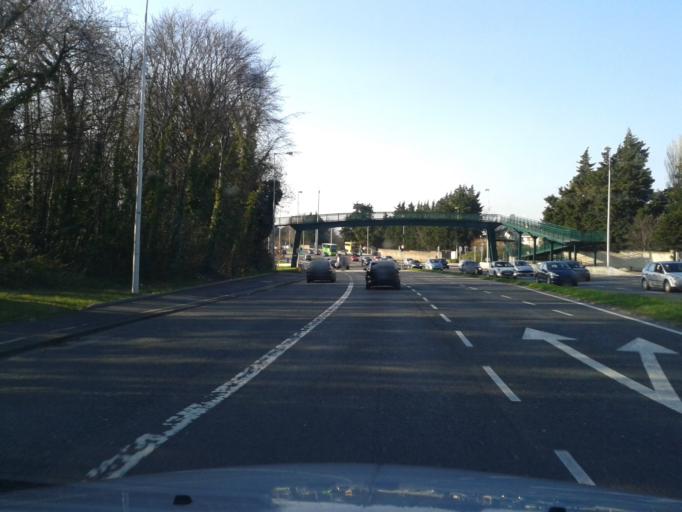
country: IE
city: Booterstown
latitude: 53.3014
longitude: -6.2063
